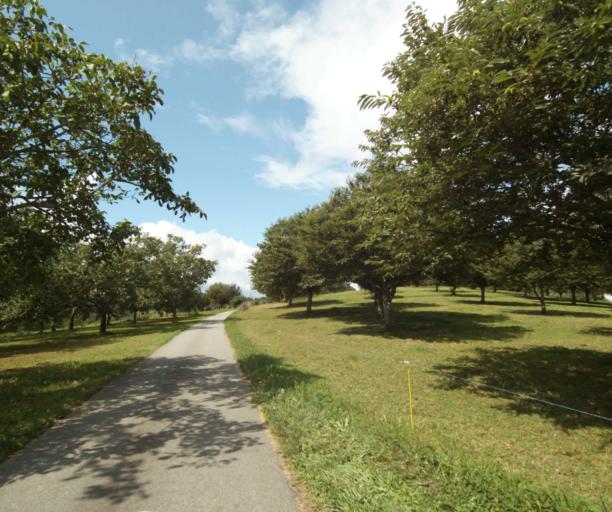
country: FR
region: Limousin
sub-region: Departement de la Correze
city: Sainte-Fortunade
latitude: 45.1728
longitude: 1.8370
